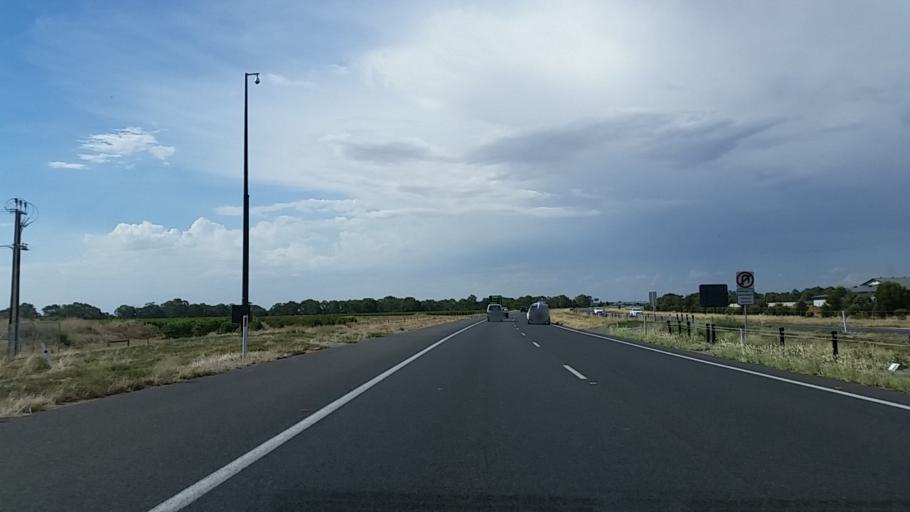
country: AU
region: South Australia
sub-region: Playford
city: Angle Vale
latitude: -34.6230
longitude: 138.6743
